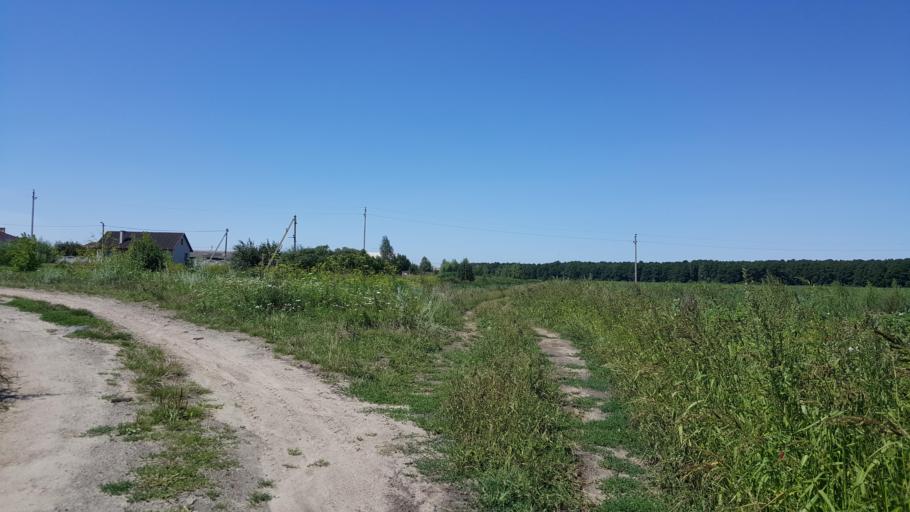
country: BY
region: Brest
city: Charnawchytsy
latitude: 52.2133
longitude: 23.7347
